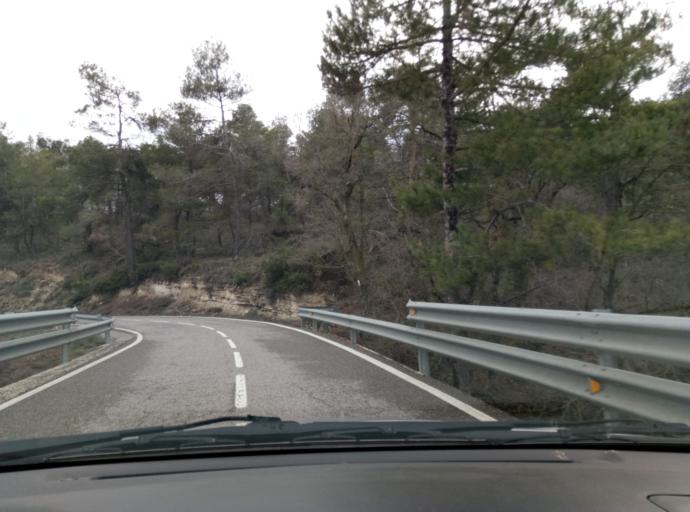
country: ES
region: Catalonia
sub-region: Provincia de Tarragona
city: Conesa
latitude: 41.5436
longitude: 1.3310
